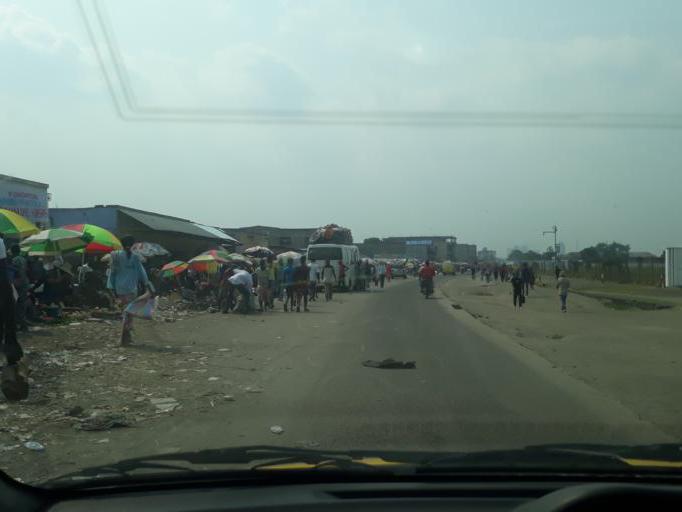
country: CD
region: Kinshasa
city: Kinshasa
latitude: -4.3305
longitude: 15.3204
